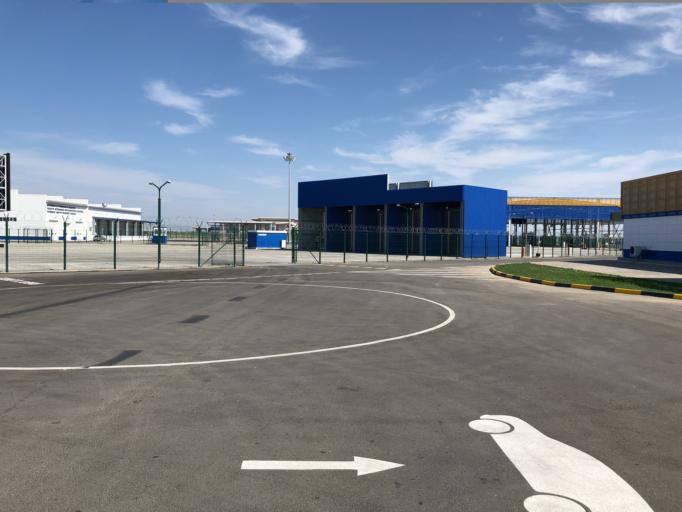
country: KZ
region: Almaty Oblysy
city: Zharkent
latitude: 44.1578
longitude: 80.3965
